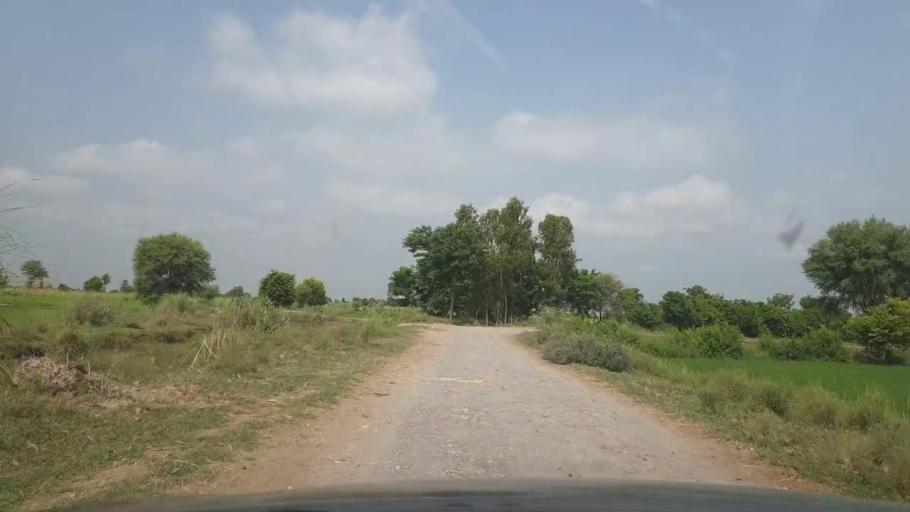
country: PK
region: Sindh
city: Ratodero
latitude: 27.8498
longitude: 68.3010
